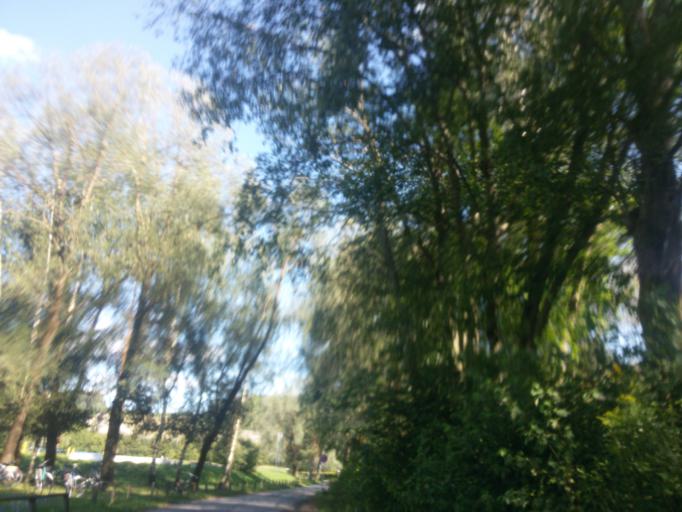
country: AT
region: Carinthia
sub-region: Politischer Bezirk Villach Land
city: Wernberg
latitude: 46.6071
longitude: 13.9053
